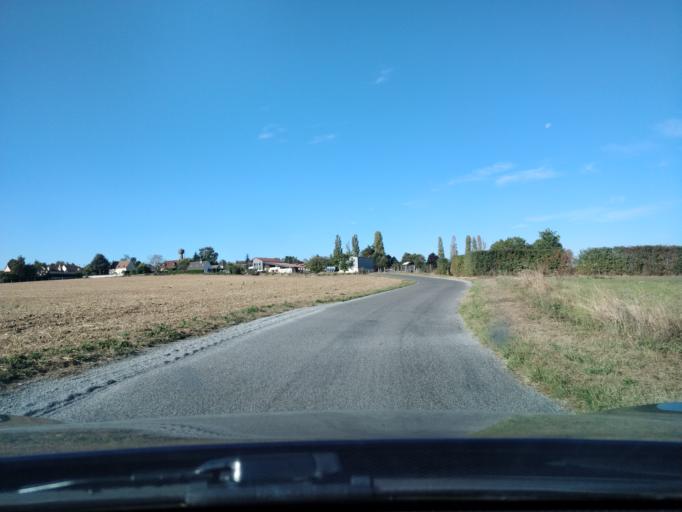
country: FR
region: Ile-de-France
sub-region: Departement de l'Essonne
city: Limours
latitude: 48.6285
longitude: 2.0788
